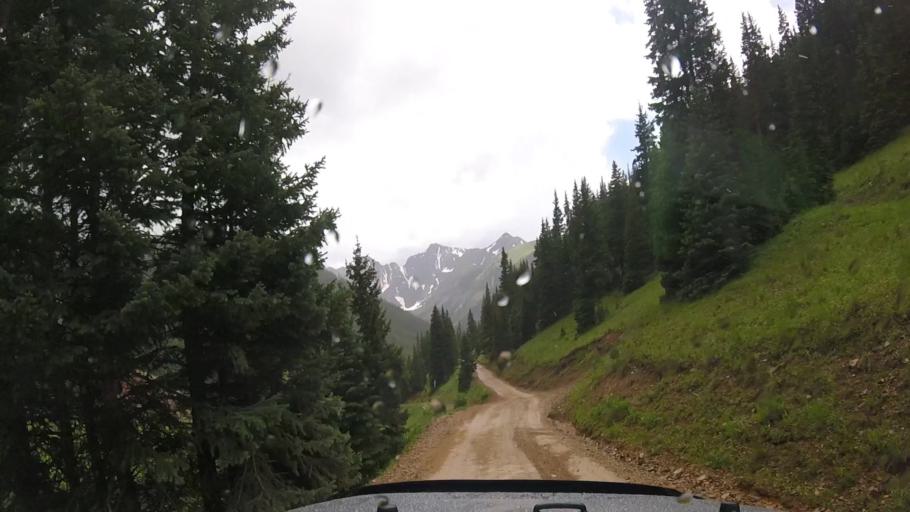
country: US
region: Colorado
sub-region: San Juan County
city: Silverton
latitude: 37.8995
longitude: -107.6469
